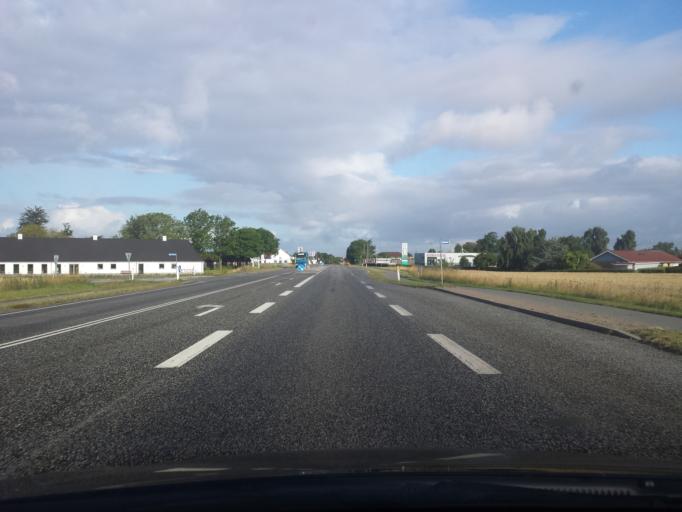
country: DK
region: South Denmark
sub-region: Sonderborg Kommune
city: Guderup
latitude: 54.9845
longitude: 9.8712
